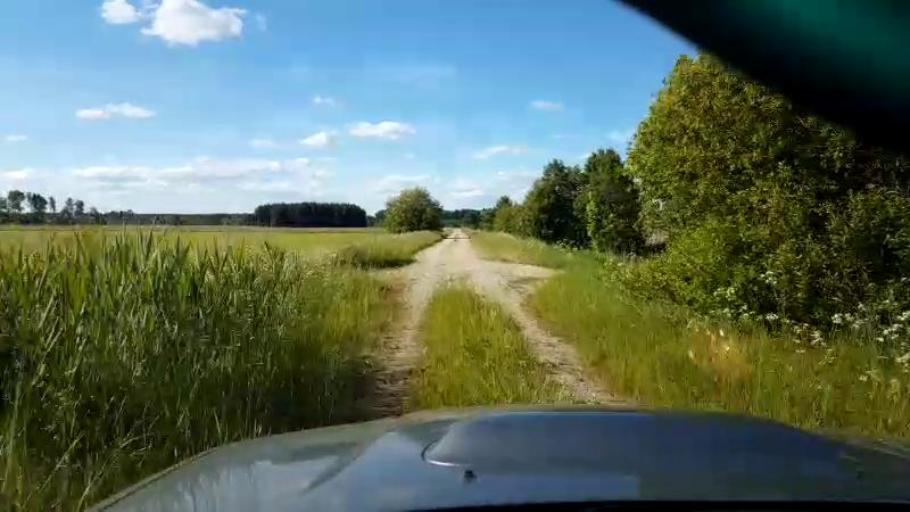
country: EE
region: Paernumaa
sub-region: Sauga vald
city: Sauga
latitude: 58.5050
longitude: 24.5905
